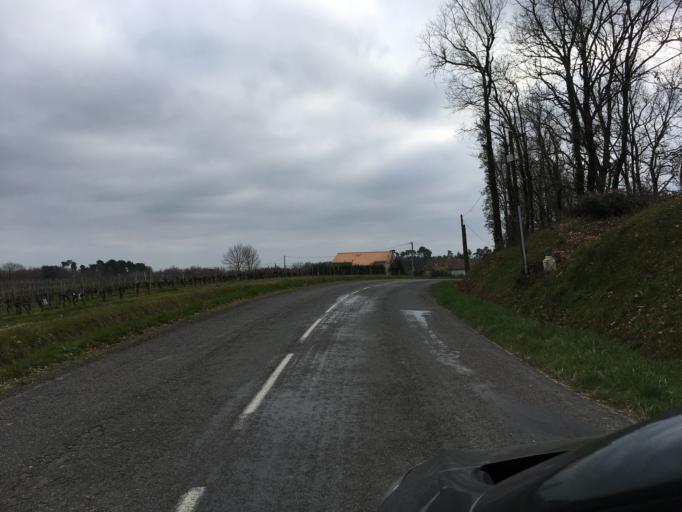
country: FR
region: Aquitaine
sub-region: Departement de la Gironde
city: Saint-Ciers-sur-Gironde
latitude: 45.3263
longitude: -0.5941
